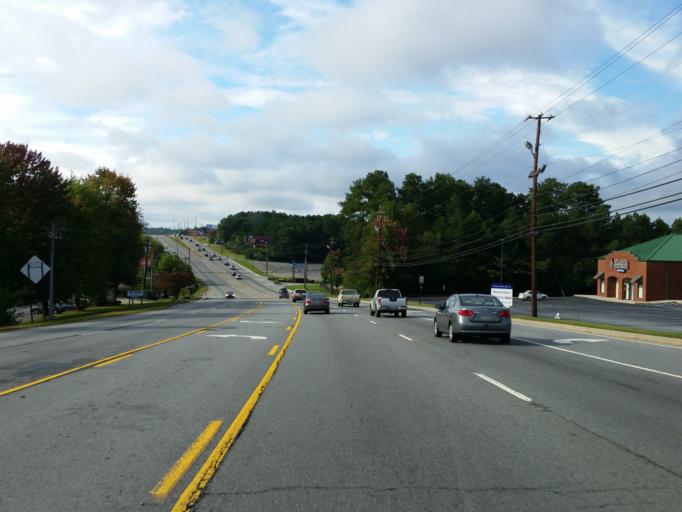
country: US
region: Georgia
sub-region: Cobb County
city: Marietta
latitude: 33.9550
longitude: -84.5228
